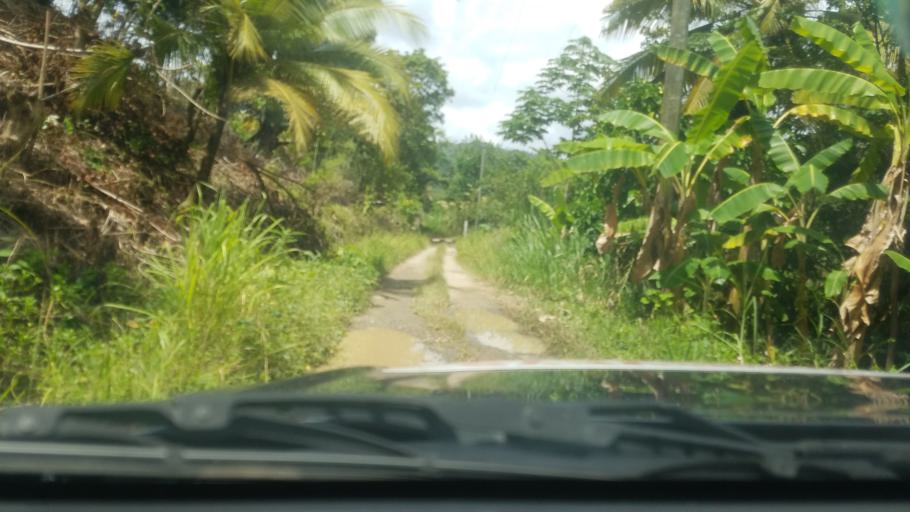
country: LC
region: Praslin
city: Praslin
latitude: 13.8688
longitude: -60.8979
